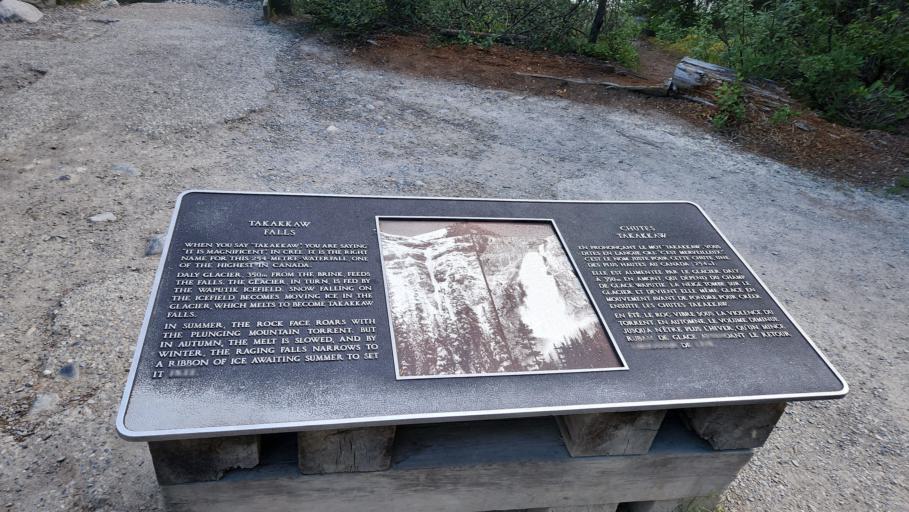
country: CA
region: Alberta
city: Lake Louise
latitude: 51.4958
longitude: -116.4806
